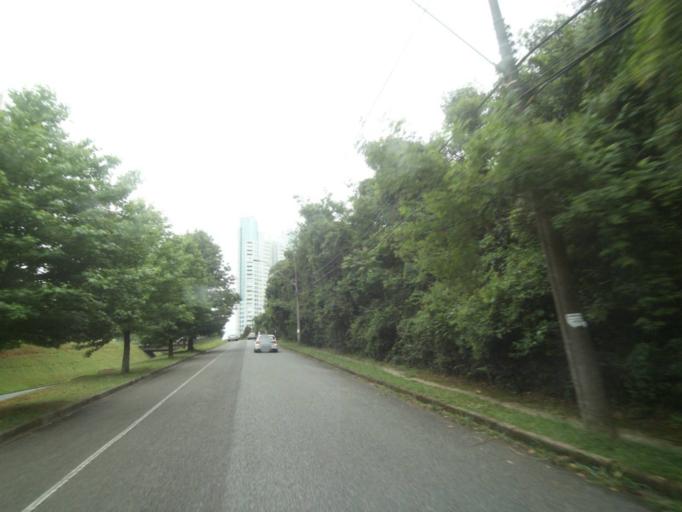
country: BR
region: Parana
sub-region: Curitiba
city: Curitiba
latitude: -25.4390
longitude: -49.3347
